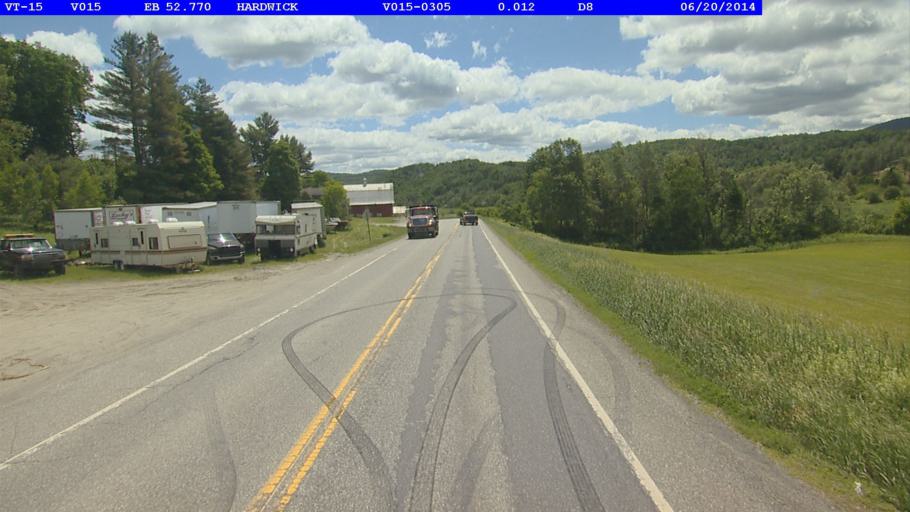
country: US
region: Vermont
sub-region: Caledonia County
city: Hardwick
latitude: 44.5248
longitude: -72.4190
